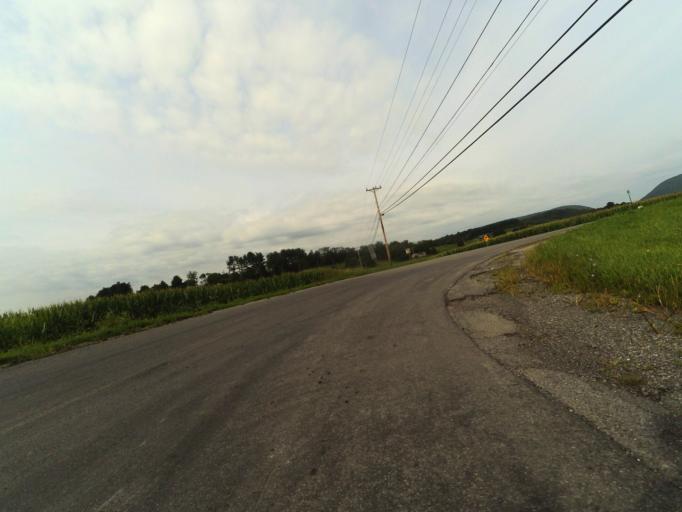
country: US
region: Pennsylvania
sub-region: Huntingdon County
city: Huntingdon
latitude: 40.5652
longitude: -78.0703
